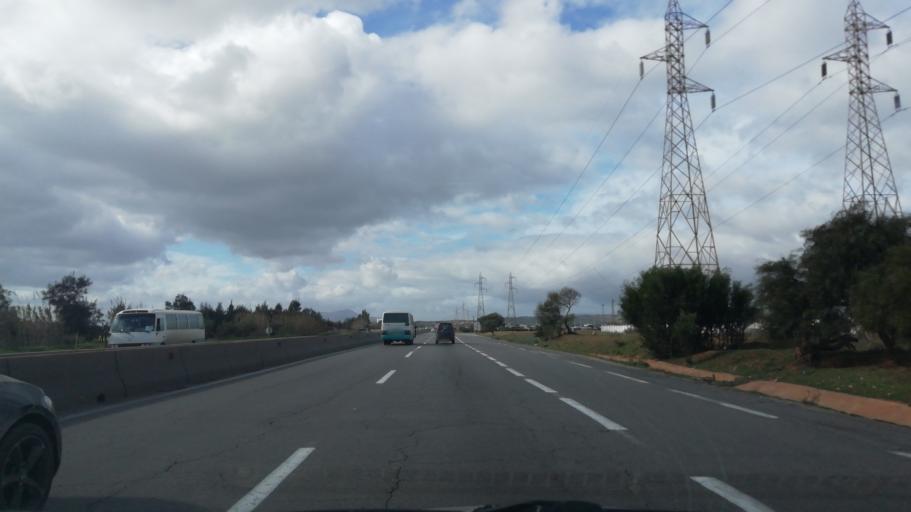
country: DZ
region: Oran
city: Ain el Bya
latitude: 35.8000
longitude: -0.3365
